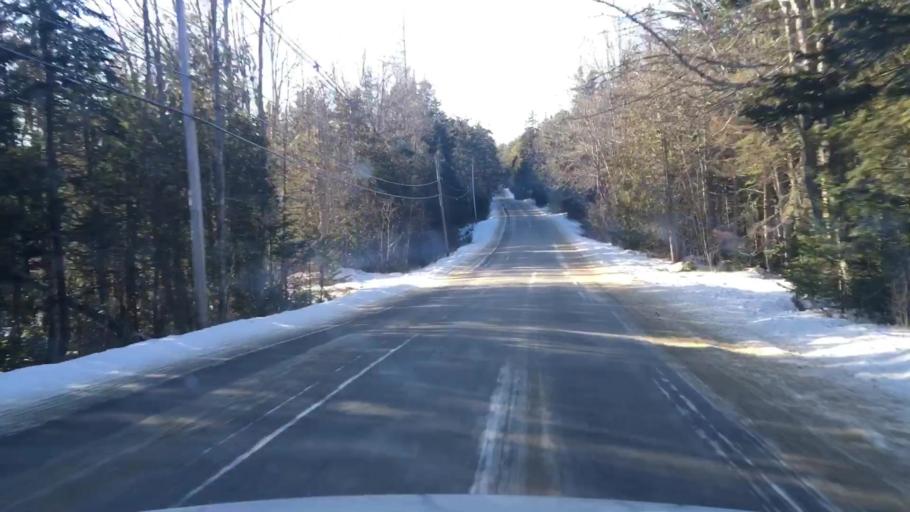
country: US
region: Maine
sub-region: Hancock County
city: Castine
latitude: 44.3597
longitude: -68.7533
